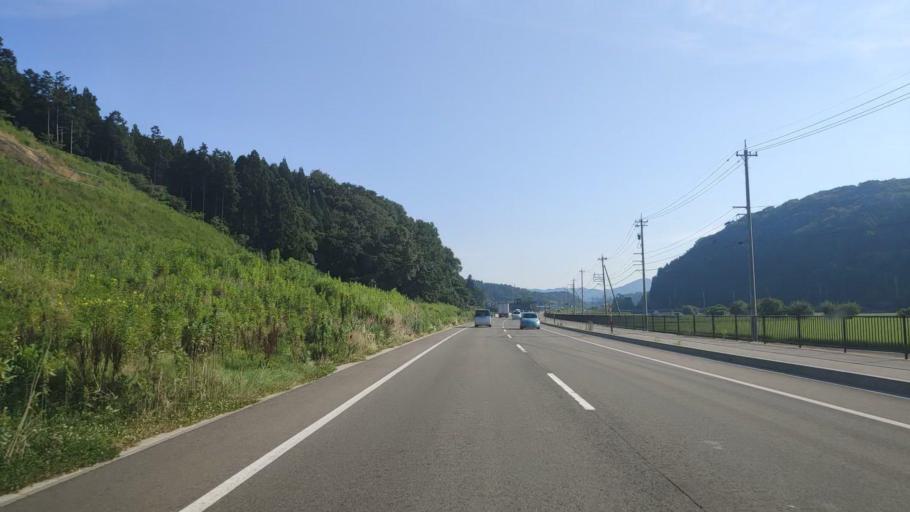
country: JP
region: Fukui
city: Maruoka
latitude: 36.2091
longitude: 136.2691
